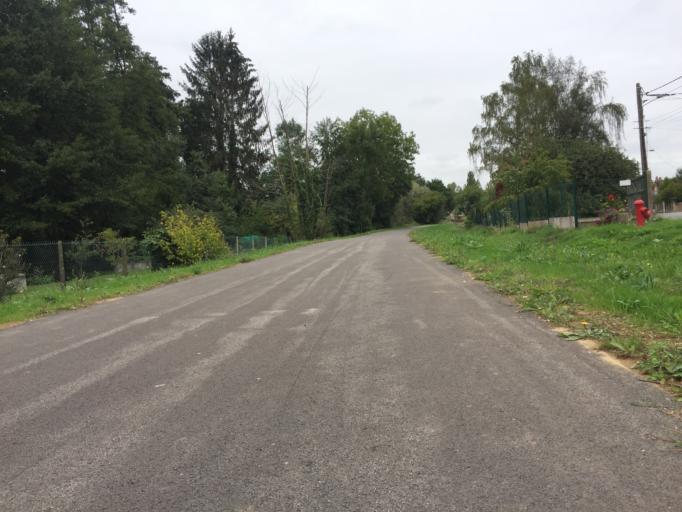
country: FR
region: Picardie
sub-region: Departement de l'Oise
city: Saint-Paul
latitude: 49.4039
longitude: 2.0087
